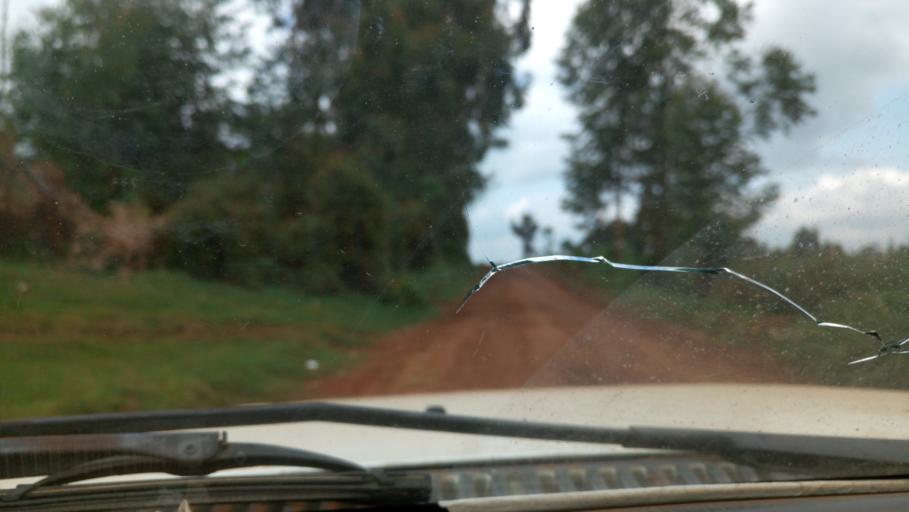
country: KE
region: Murang'a District
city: Kangema
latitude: -0.7568
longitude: 36.8858
